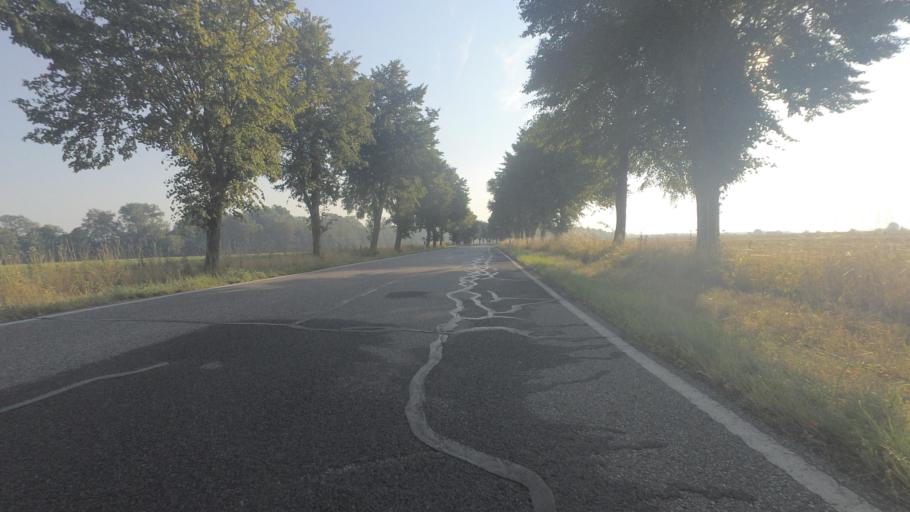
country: DE
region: Mecklenburg-Vorpommern
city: Demmin
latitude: 53.9567
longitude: 13.1185
